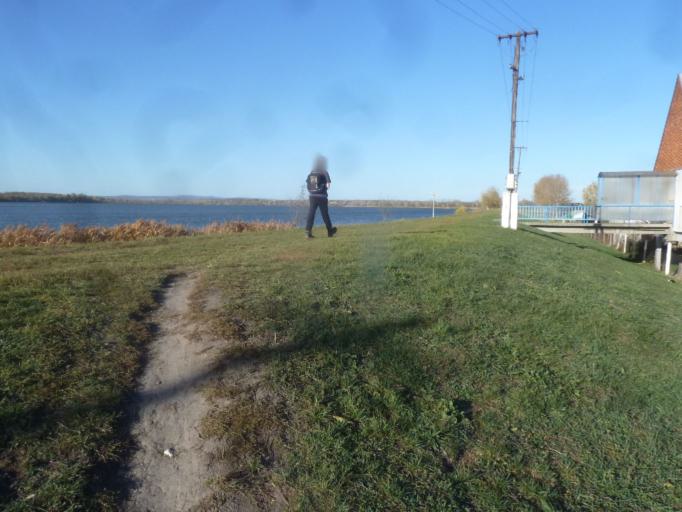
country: HU
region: Fejer
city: Pakozd
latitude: 47.2512
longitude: 18.4892
